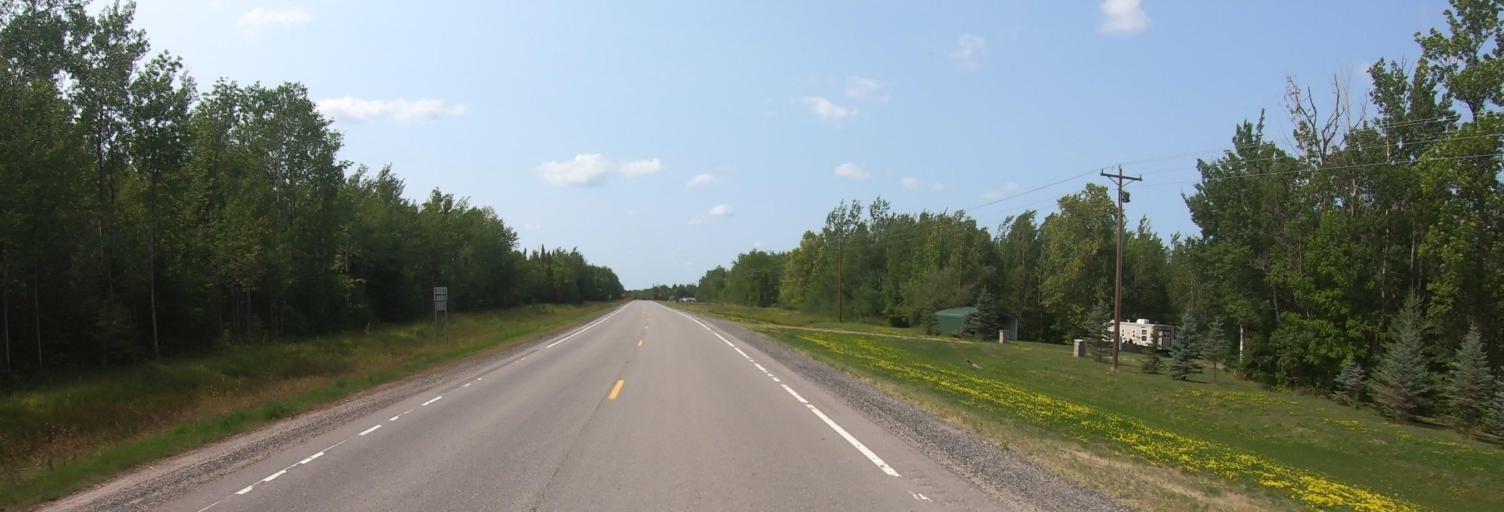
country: US
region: Minnesota
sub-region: Lake of the Woods County
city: Baudette
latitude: 48.6945
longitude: -94.4742
